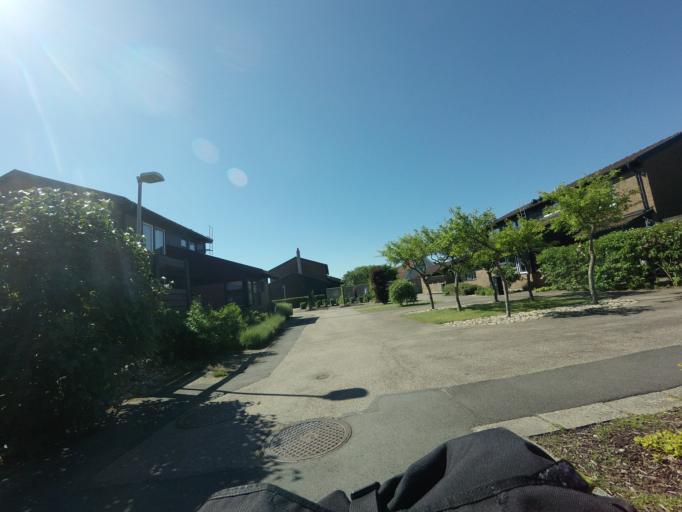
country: SE
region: Skane
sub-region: Hoganas Kommun
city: Hoganas
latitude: 56.1744
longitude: 12.5667
